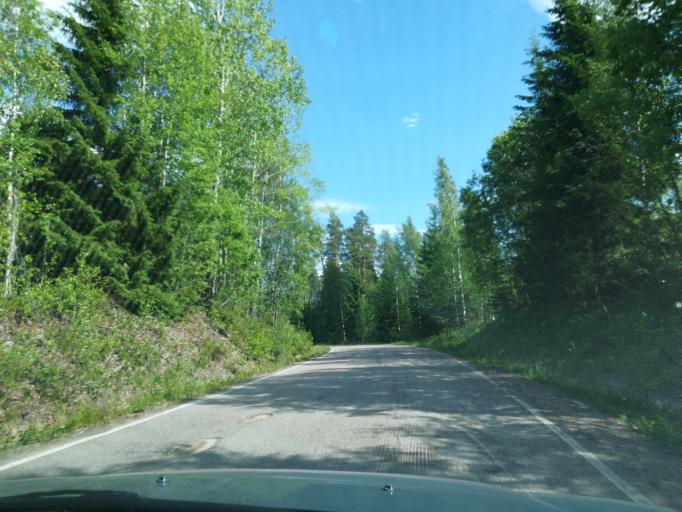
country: FI
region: South Karelia
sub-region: Imatra
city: Ruokolahti
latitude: 61.4727
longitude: 28.8595
